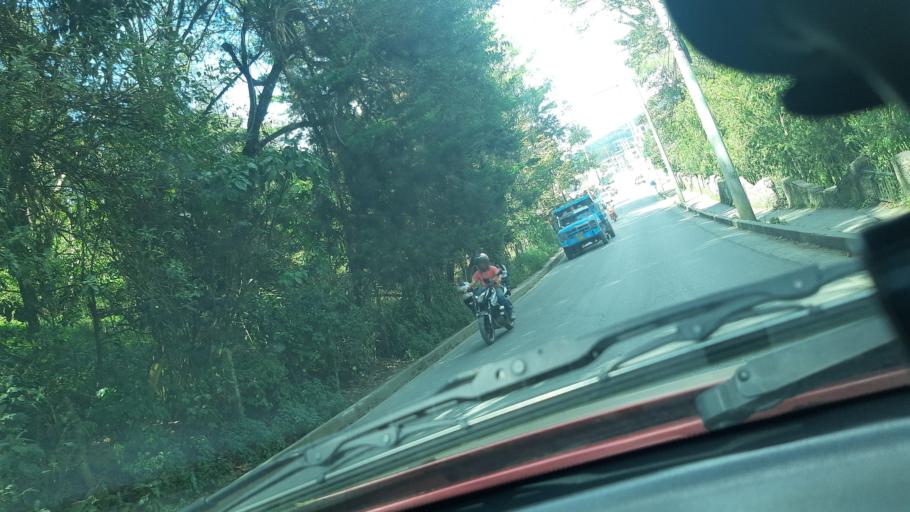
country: CO
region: Boyaca
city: Moniquira
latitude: 5.8712
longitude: -73.5737
